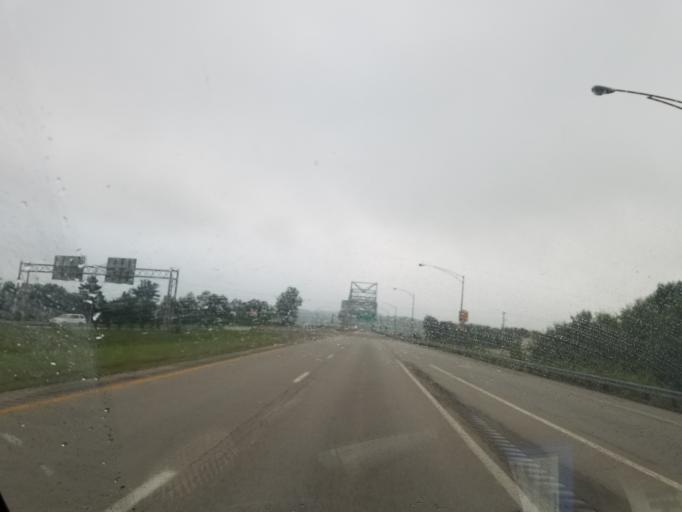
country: US
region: West Virginia
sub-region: Mason County
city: Point Pleasant
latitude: 38.8385
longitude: -82.1533
